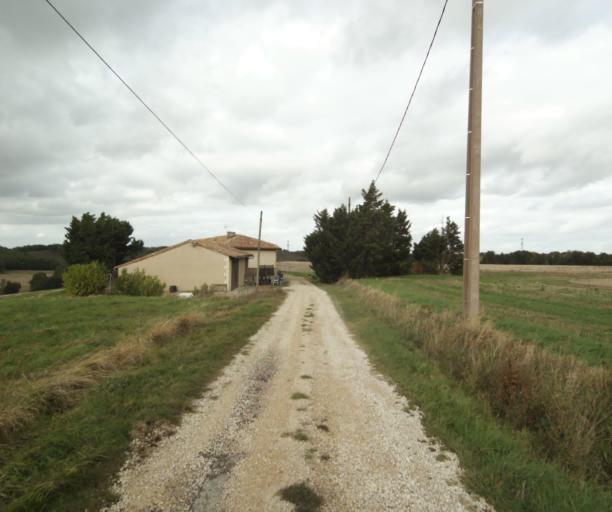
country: FR
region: Midi-Pyrenees
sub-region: Departement du Tarn-et-Garonne
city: Beaumont-de-Lomagne
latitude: 43.9027
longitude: 1.0905
